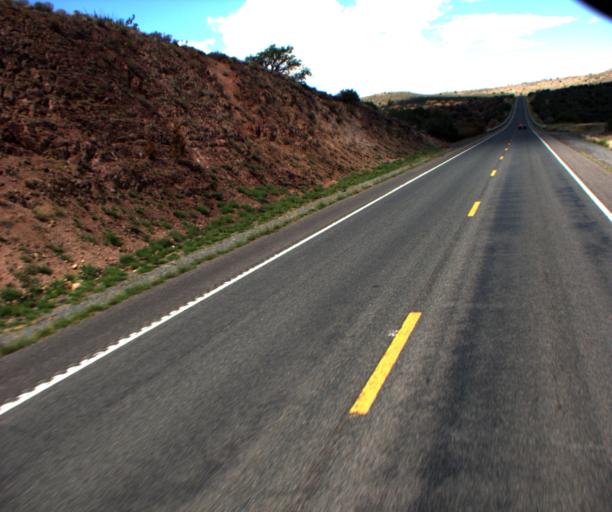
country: US
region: Arizona
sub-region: Yavapai County
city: Camp Verde
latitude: 34.5186
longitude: -112.0310
